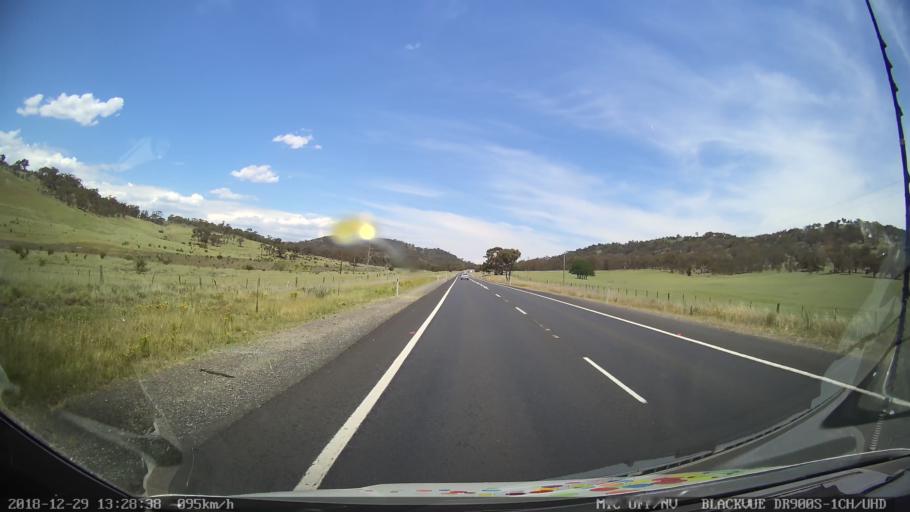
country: AU
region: New South Wales
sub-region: Cooma-Monaro
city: Cooma
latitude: -35.8787
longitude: 149.1607
